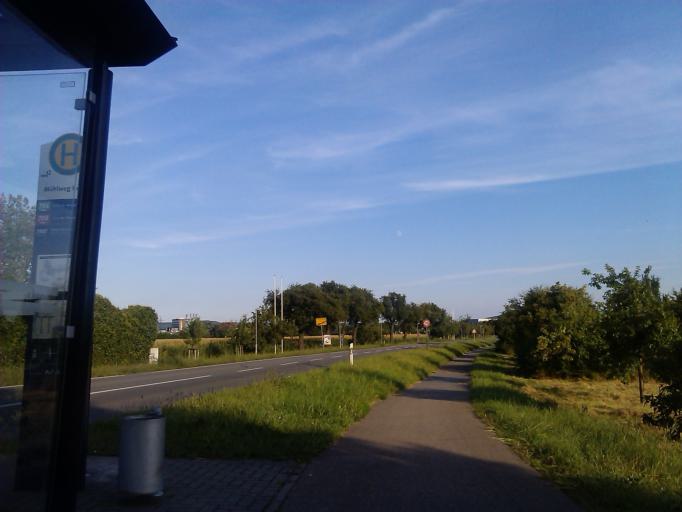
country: DE
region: Baden-Wuerttemberg
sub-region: Karlsruhe Region
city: Walldorf
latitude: 49.2975
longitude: 8.6511
